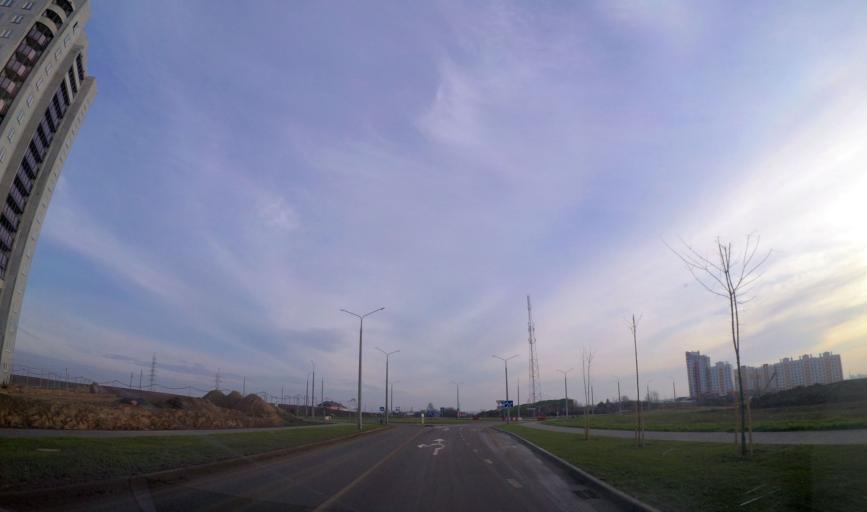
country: BY
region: Grodnenskaya
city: Hrodna
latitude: 53.7166
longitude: 23.8672
